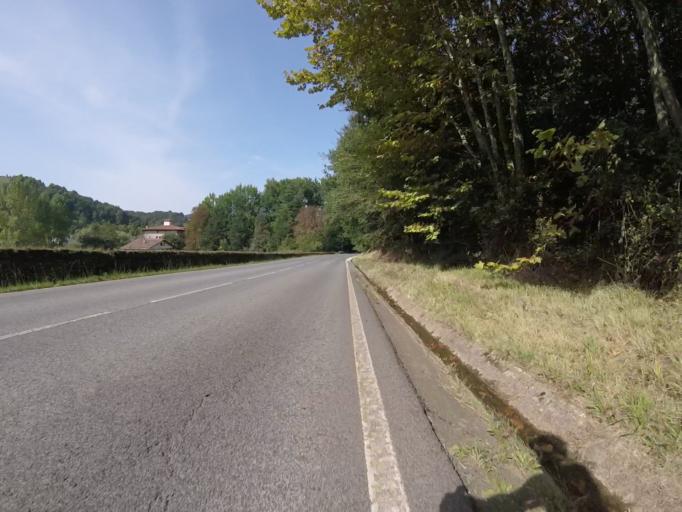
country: ES
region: Navarre
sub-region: Provincia de Navarra
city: Doneztebe
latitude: 43.1316
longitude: -1.6548
